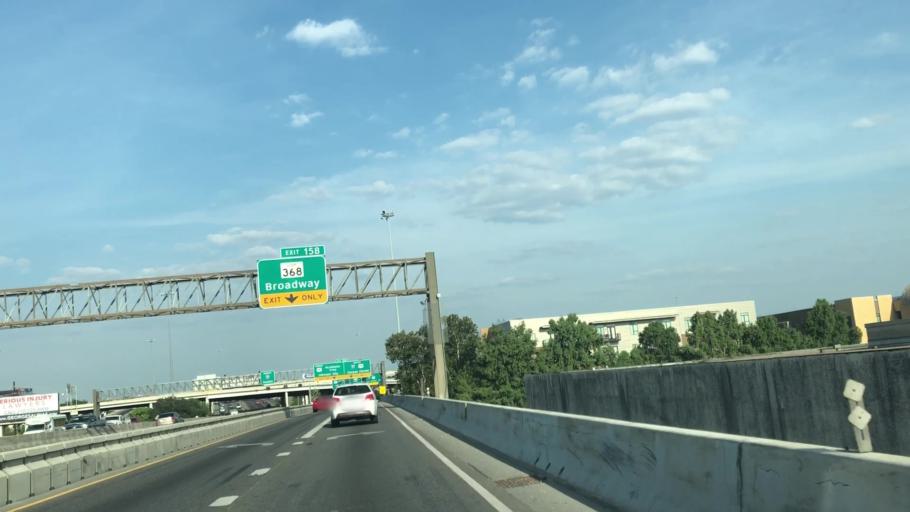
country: US
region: Texas
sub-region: Bexar County
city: San Antonio
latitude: 29.4399
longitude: -98.4828
